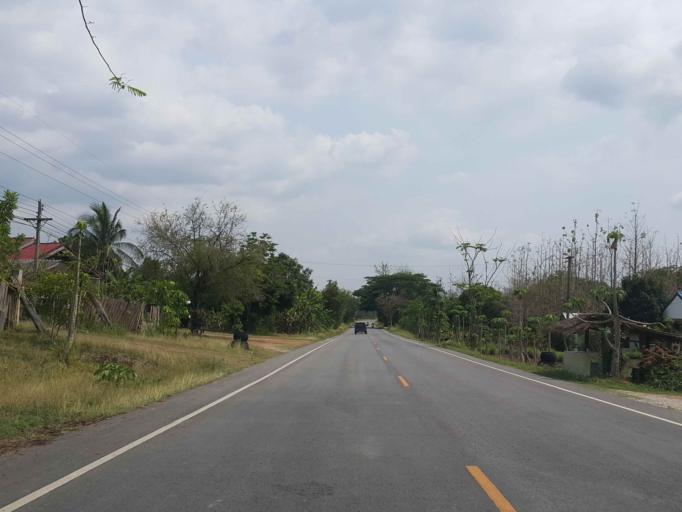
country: TH
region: Lampang
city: Thoen
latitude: 17.5068
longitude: 99.3507
